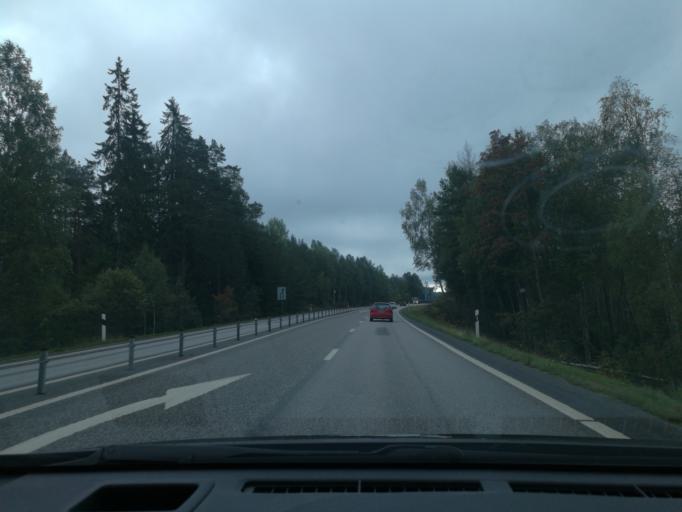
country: SE
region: OEstergoetland
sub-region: Norrkopings Kommun
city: Jursla
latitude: 58.7648
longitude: 16.1706
